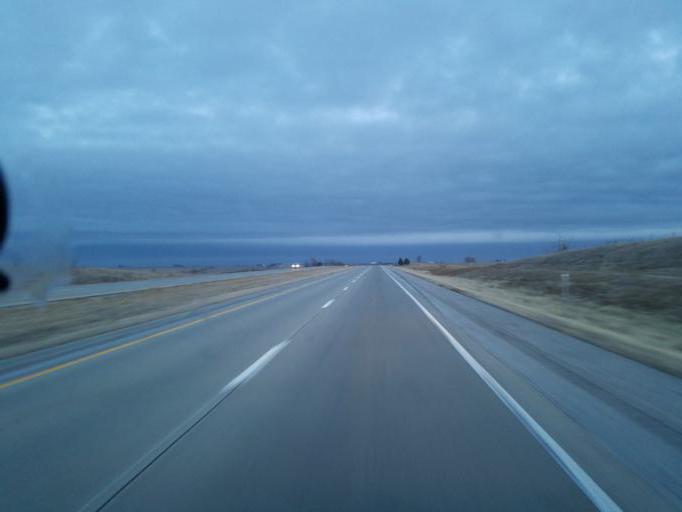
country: US
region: Iowa
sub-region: Cass County
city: Atlantic
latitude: 41.4981
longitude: -95.1628
